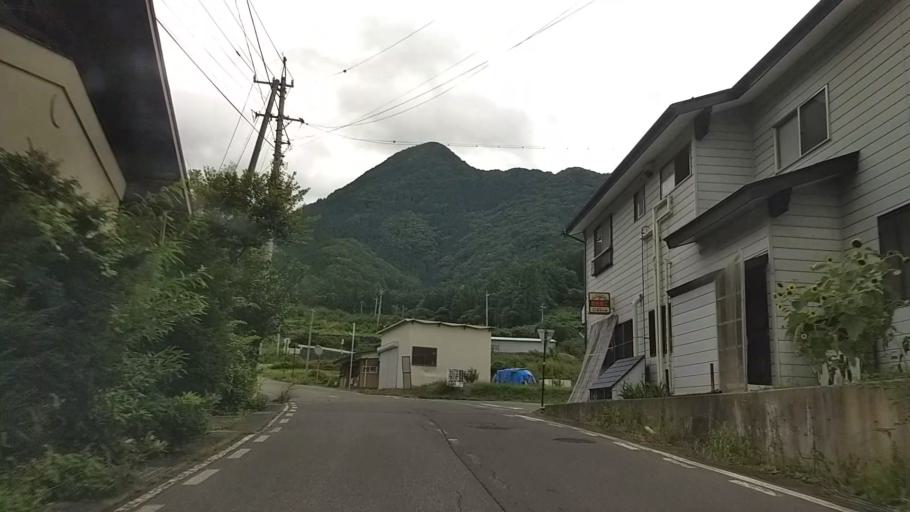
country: JP
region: Nagano
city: Iiyama
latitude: 36.8171
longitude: 138.3642
